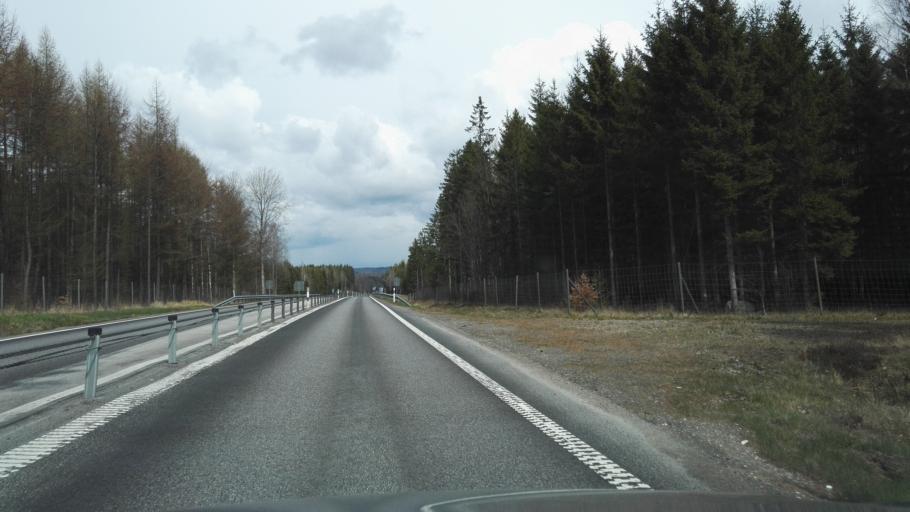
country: SE
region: Kronoberg
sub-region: Vaxjo Kommun
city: Rottne
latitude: 56.9616
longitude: 14.9517
